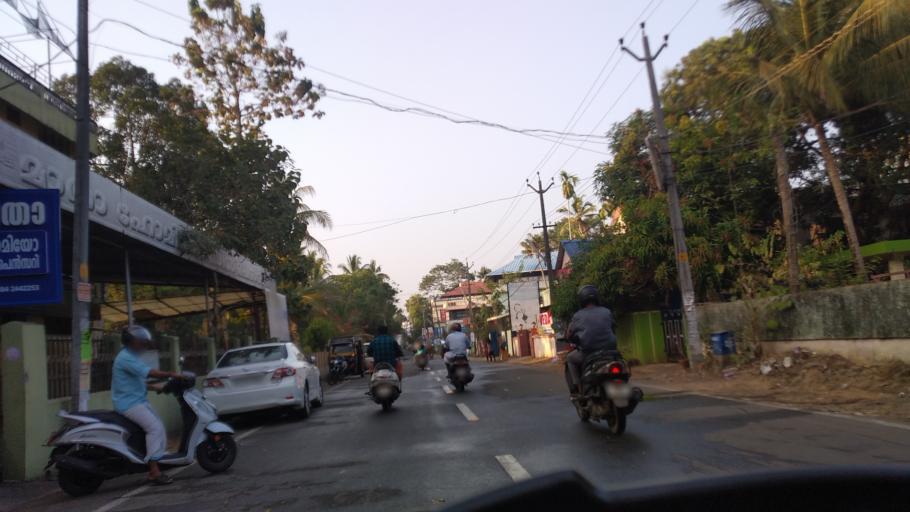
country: IN
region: Kerala
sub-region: Thrissur District
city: Kodungallur
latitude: 10.1495
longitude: 76.2265
